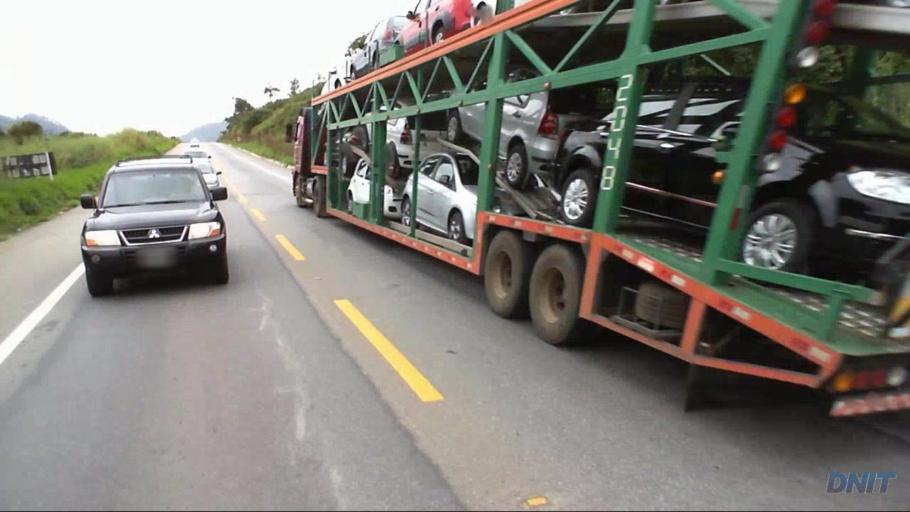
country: BR
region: Minas Gerais
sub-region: Timoteo
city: Timoteo
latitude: -19.6019
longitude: -42.7552
